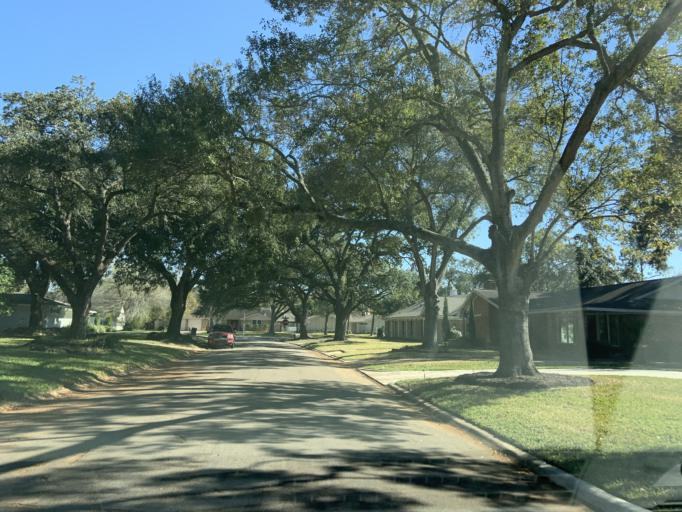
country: US
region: Texas
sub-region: Harris County
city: Bellaire
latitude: 29.6780
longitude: -95.5153
